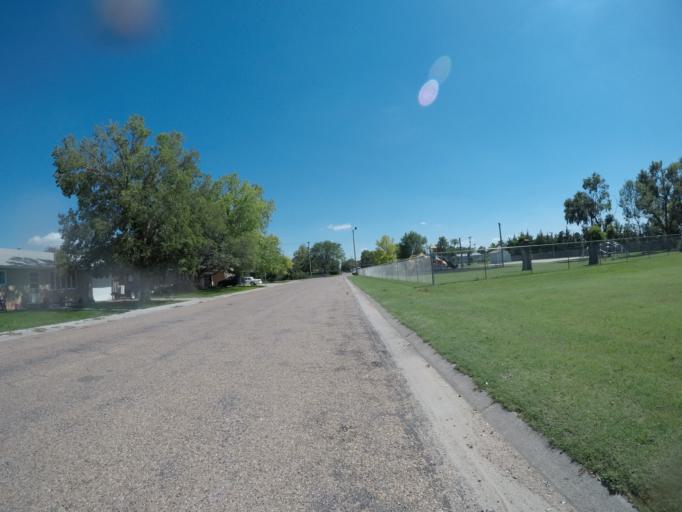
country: US
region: Kansas
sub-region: Sheridan County
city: Hoxie
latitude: 39.3595
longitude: -100.4372
